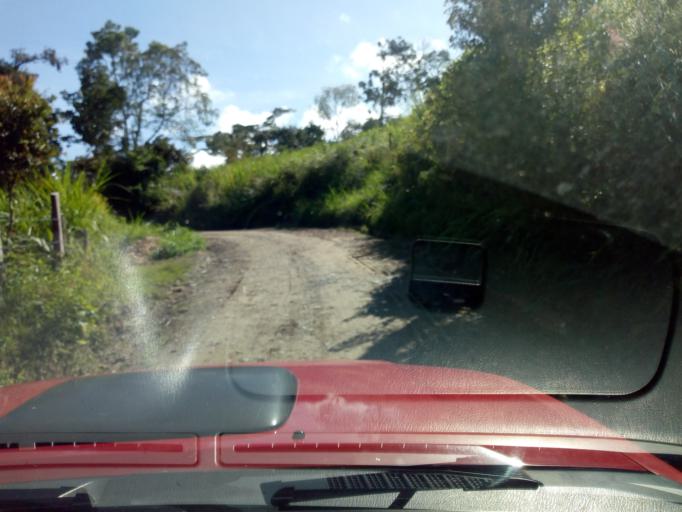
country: CO
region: Boyaca
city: Moniquira
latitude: 5.8938
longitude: -73.5267
